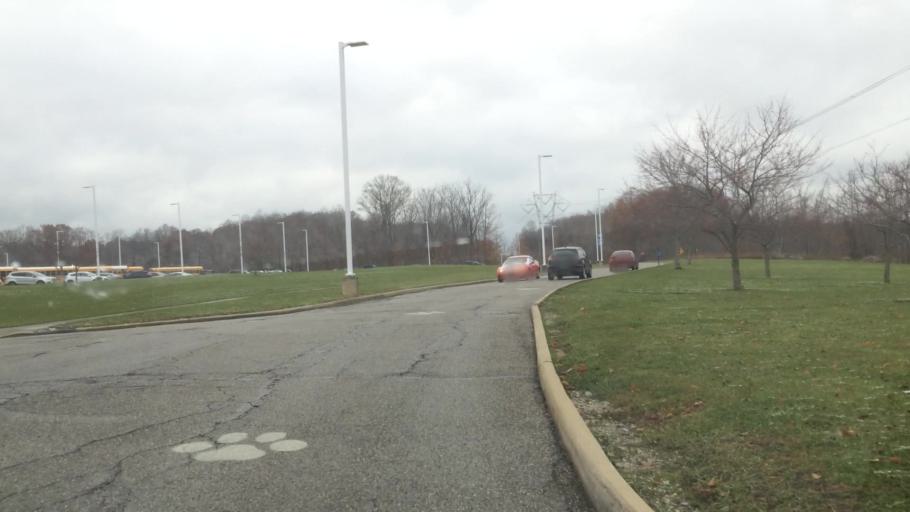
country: US
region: Ohio
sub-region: Summit County
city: Twinsburg
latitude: 41.3189
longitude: -81.4507
